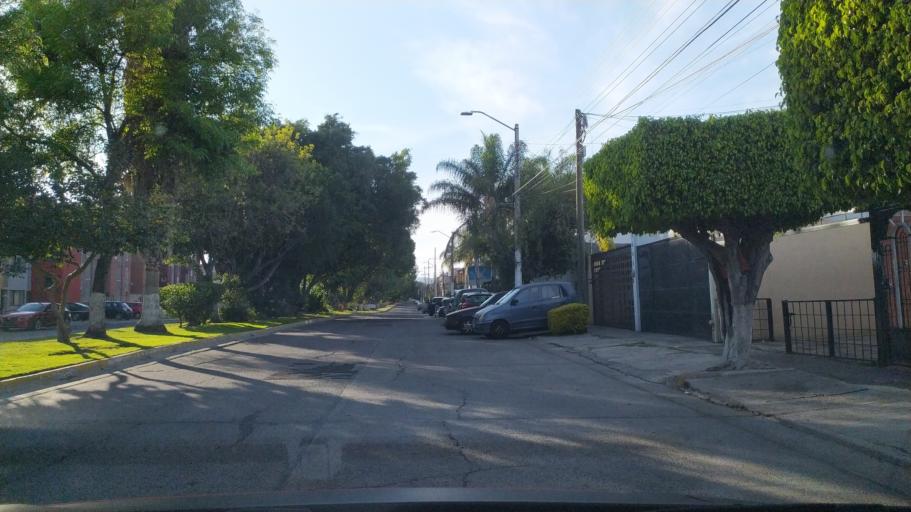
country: MX
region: Jalisco
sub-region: Tlajomulco de Zuniga
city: La Tijera
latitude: 20.6262
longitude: -103.4214
